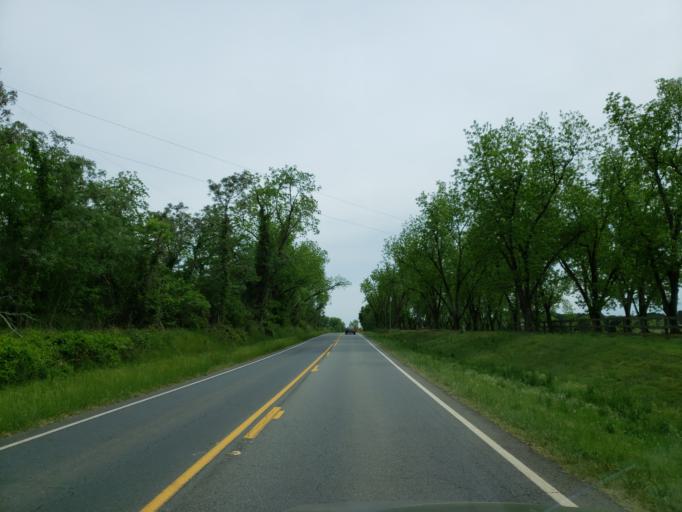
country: US
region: Georgia
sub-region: Macon County
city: Marshallville
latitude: 32.3939
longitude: -83.8669
